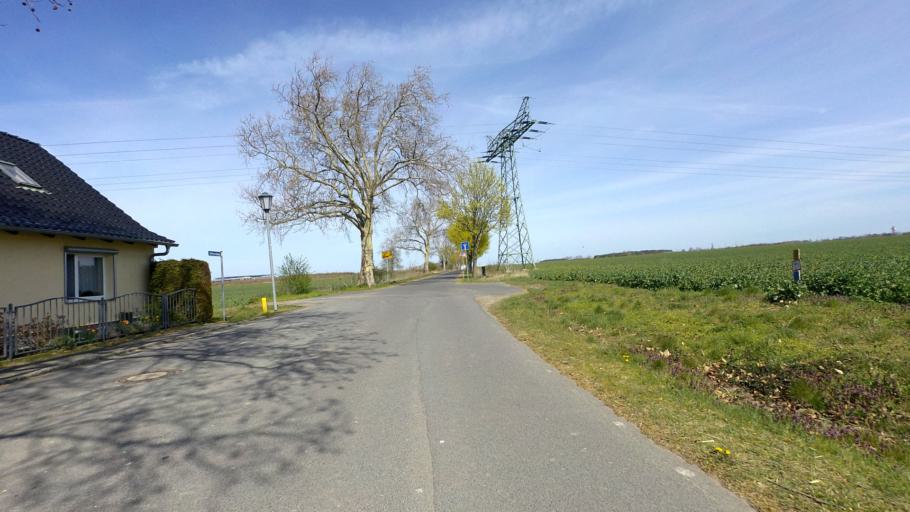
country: DE
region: Brandenburg
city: Schonefeld
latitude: 52.3452
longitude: 13.5110
